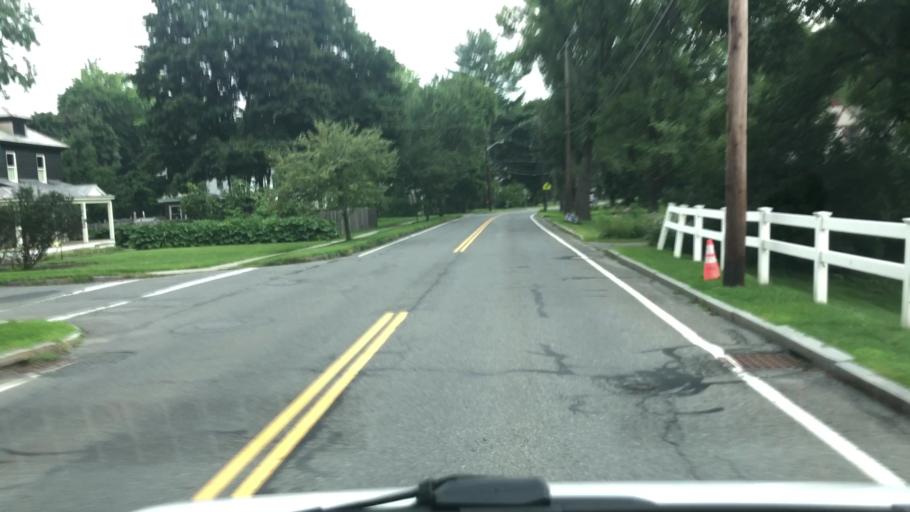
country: US
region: Massachusetts
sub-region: Berkshire County
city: Williamstown
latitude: 42.7130
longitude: -73.1960
